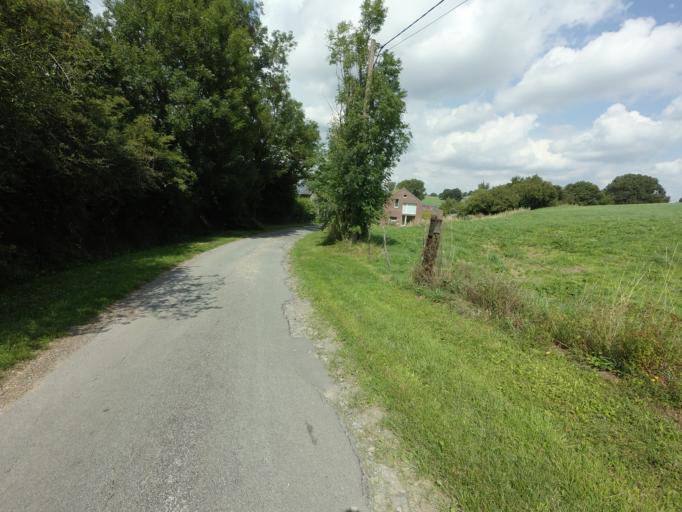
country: BE
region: Wallonia
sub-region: Province de Liege
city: Lontzen
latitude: 50.6993
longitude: 5.9839
